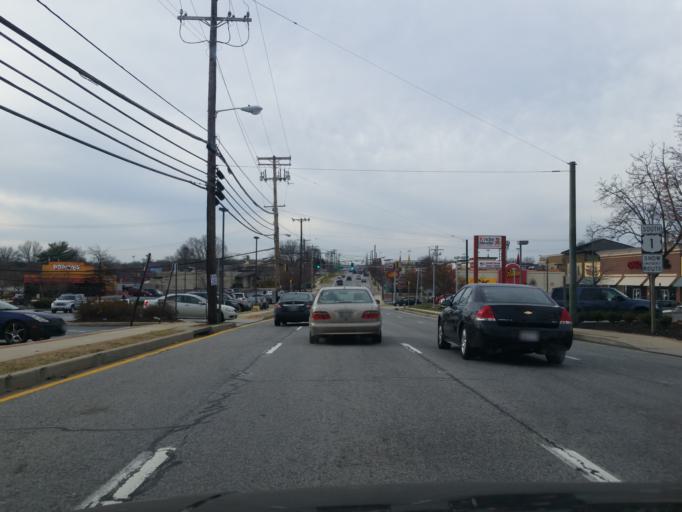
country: US
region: Maryland
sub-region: Prince George's County
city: Laurel
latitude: 39.0980
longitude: -76.8499
